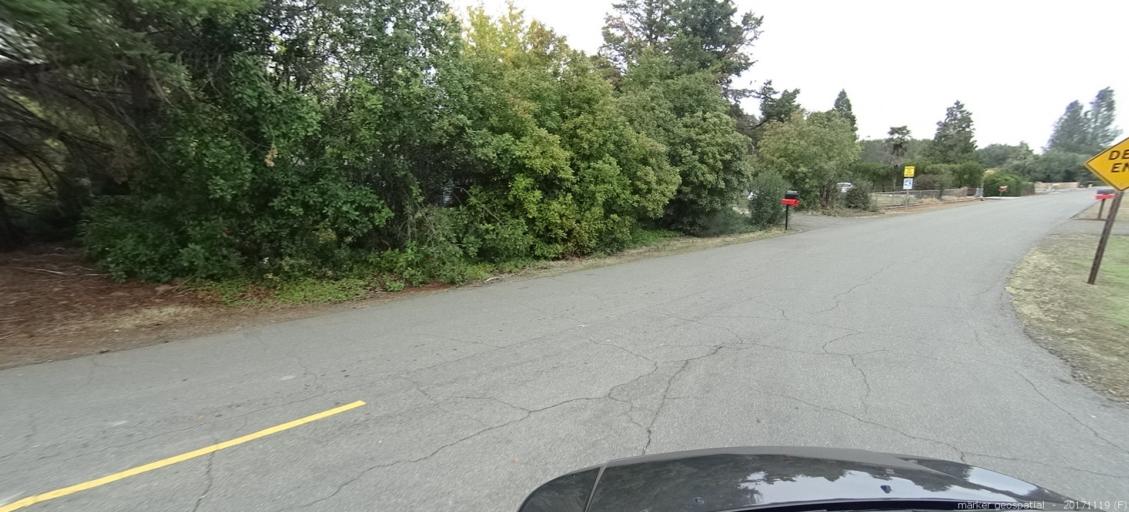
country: US
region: California
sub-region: Shasta County
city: Redding
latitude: 40.4876
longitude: -122.4166
